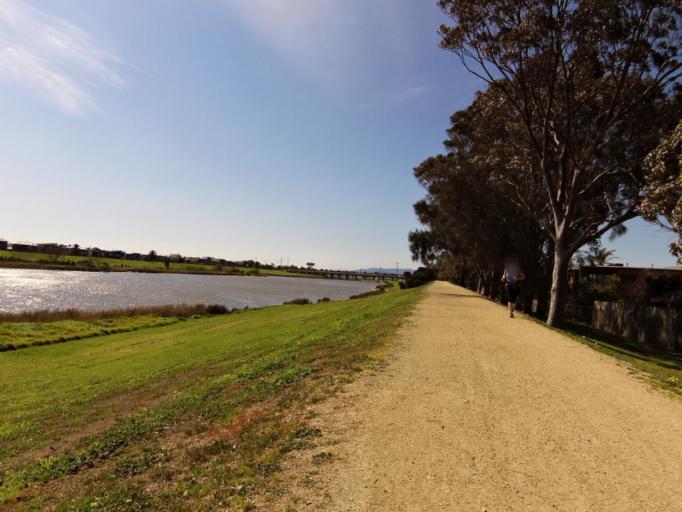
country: AU
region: Victoria
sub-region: Kingston
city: Patterson Lakes
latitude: -38.0630
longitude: 145.1434
